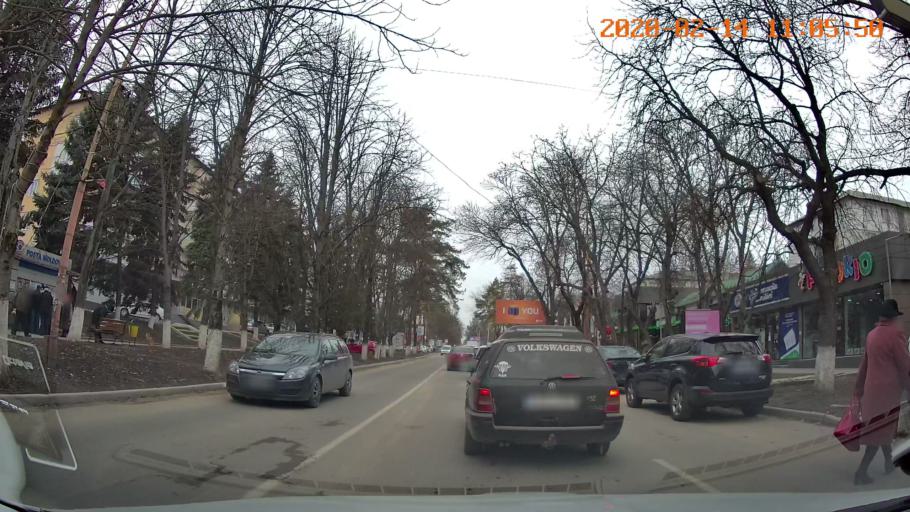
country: MD
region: Raionul Edinet
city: Edinet
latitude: 48.1682
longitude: 27.3078
